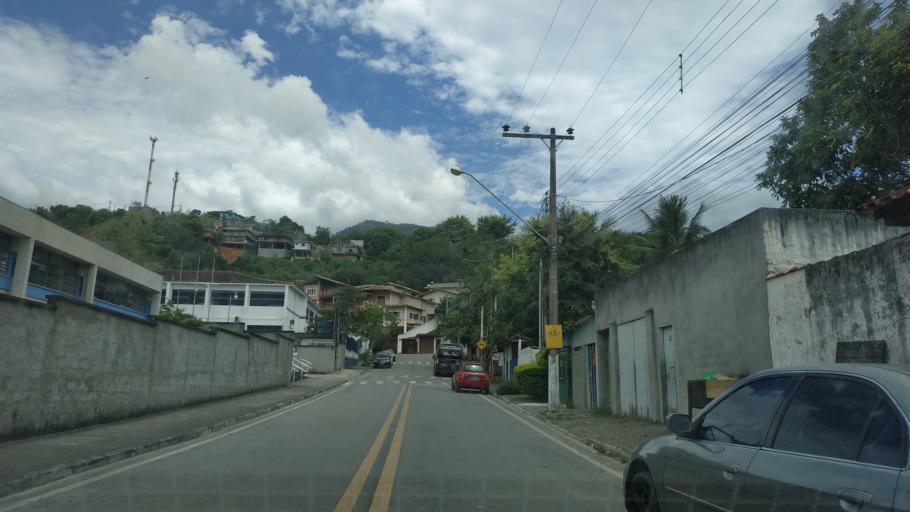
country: BR
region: Sao Paulo
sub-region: Ilhabela
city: Ilhabela
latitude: -23.8249
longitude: -45.3583
